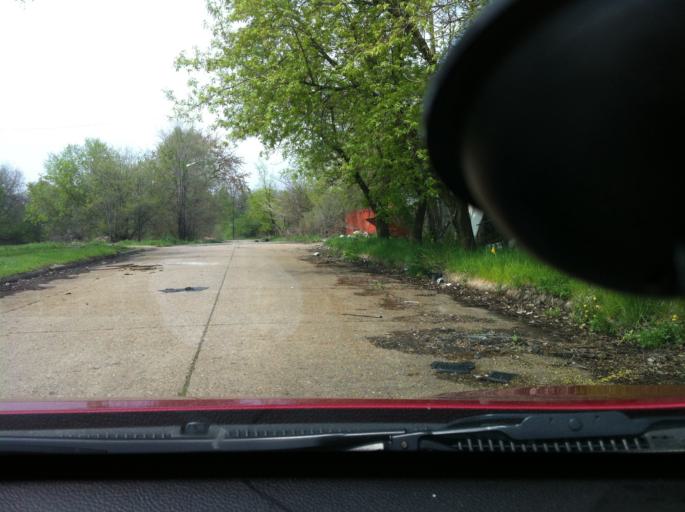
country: US
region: Michigan
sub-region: Wayne County
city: River Rouge
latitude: 42.3046
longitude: -83.0950
